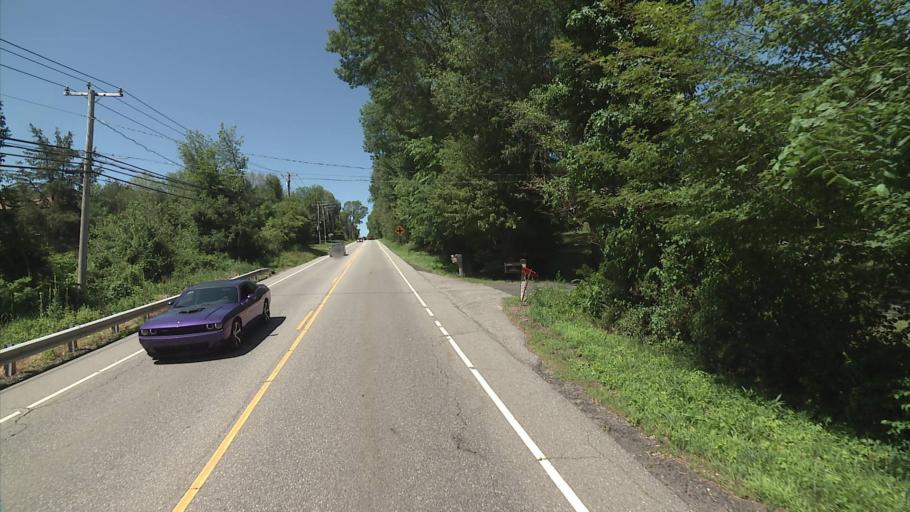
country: US
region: Connecticut
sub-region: New London County
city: Colchester
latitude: 41.5656
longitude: -72.3495
